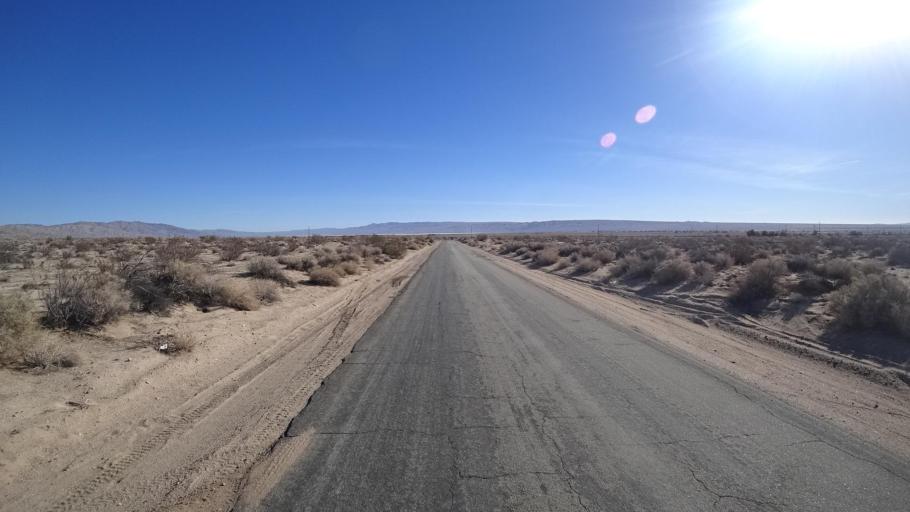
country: US
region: California
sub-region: Kern County
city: California City
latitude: 35.3013
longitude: -117.9889
